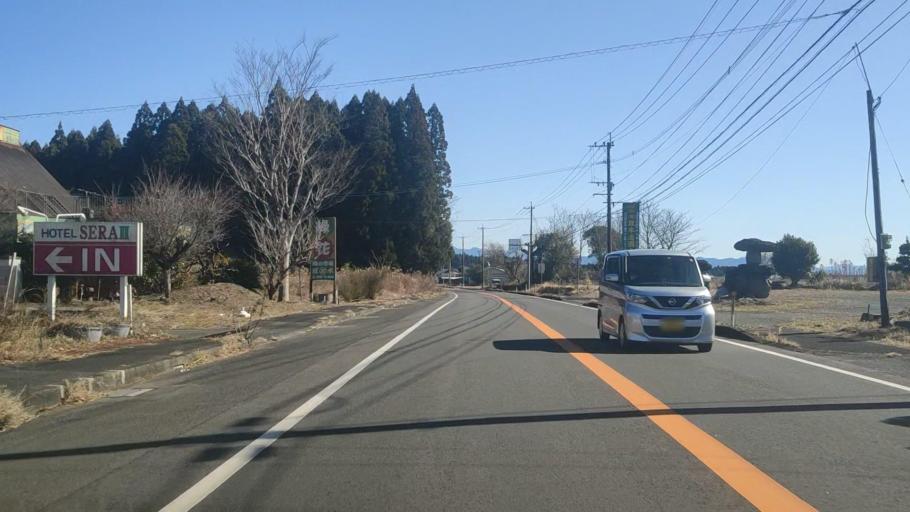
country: JP
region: Kagoshima
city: Sueyoshicho-ninokata
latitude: 31.6945
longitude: 130.9808
